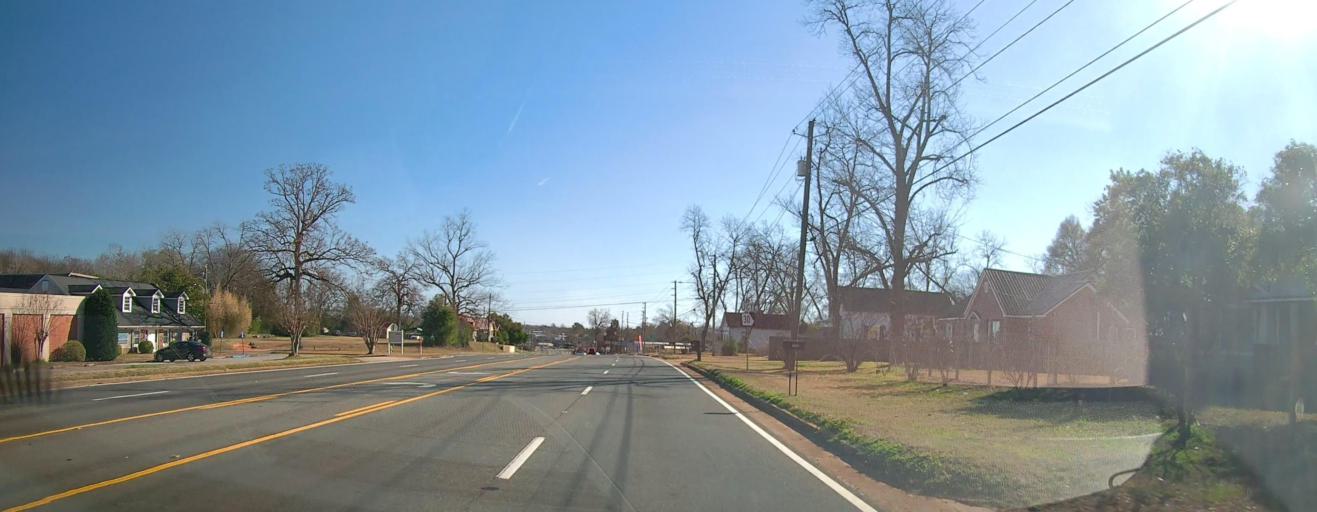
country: US
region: Georgia
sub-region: Sumter County
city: Americus
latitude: 32.0880
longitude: -84.2404
